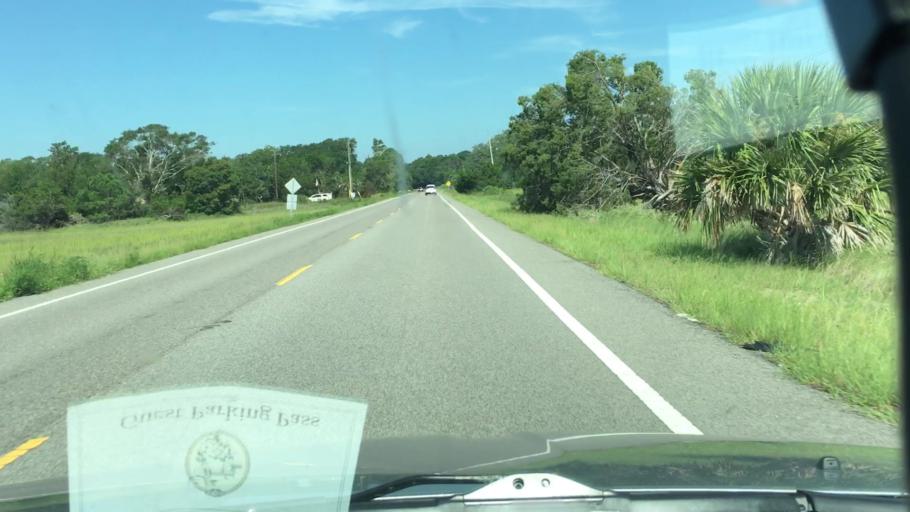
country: US
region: South Carolina
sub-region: Beaufort County
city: Beaufort
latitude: 32.4126
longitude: -80.4765
